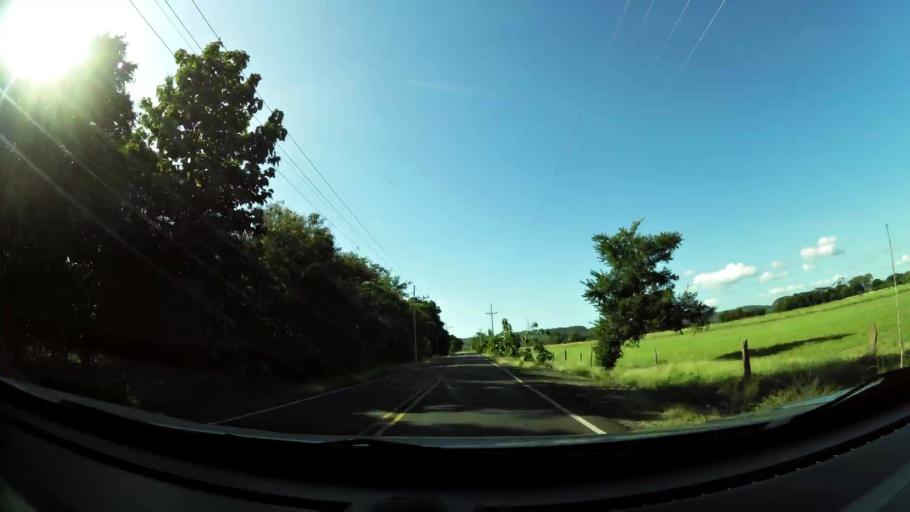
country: CR
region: Guanacaste
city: Sardinal
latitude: 10.5657
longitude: -85.5960
